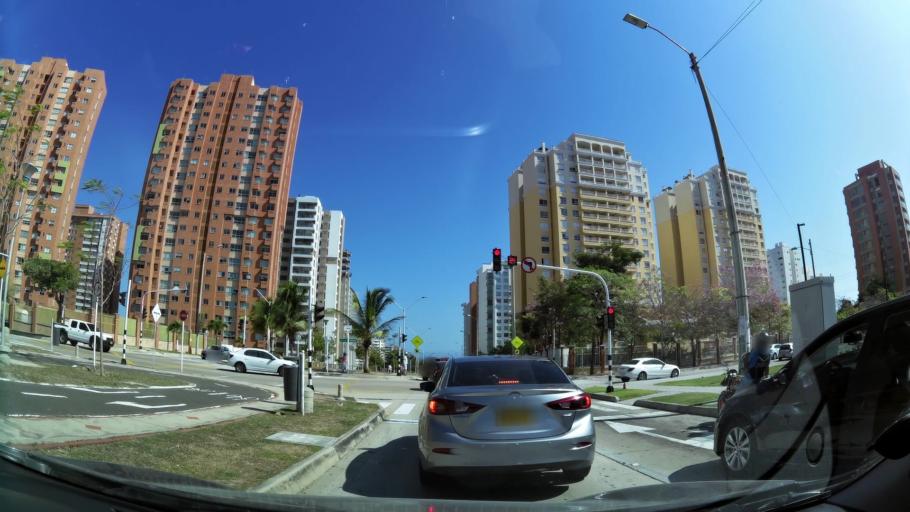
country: CO
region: Atlantico
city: Barranquilla
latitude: 11.0159
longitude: -74.8264
